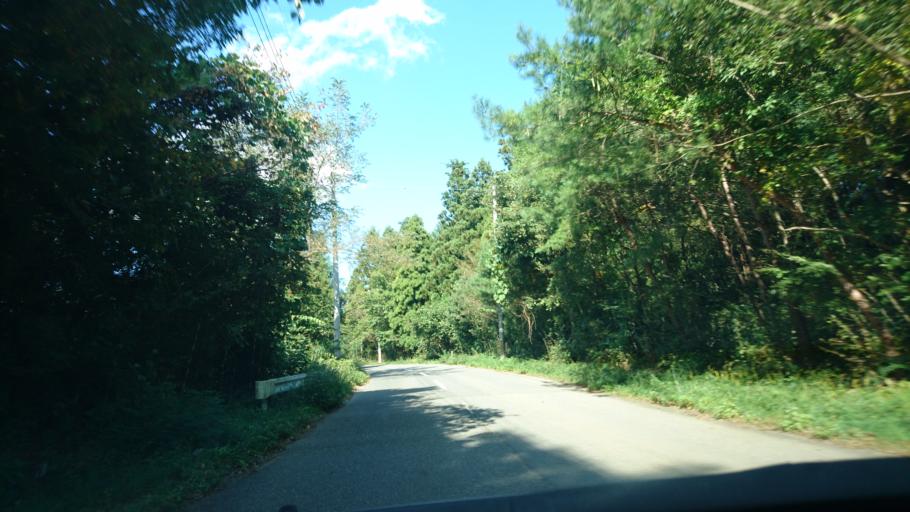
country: JP
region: Iwate
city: Ichinoseki
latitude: 38.8713
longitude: 141.0442
